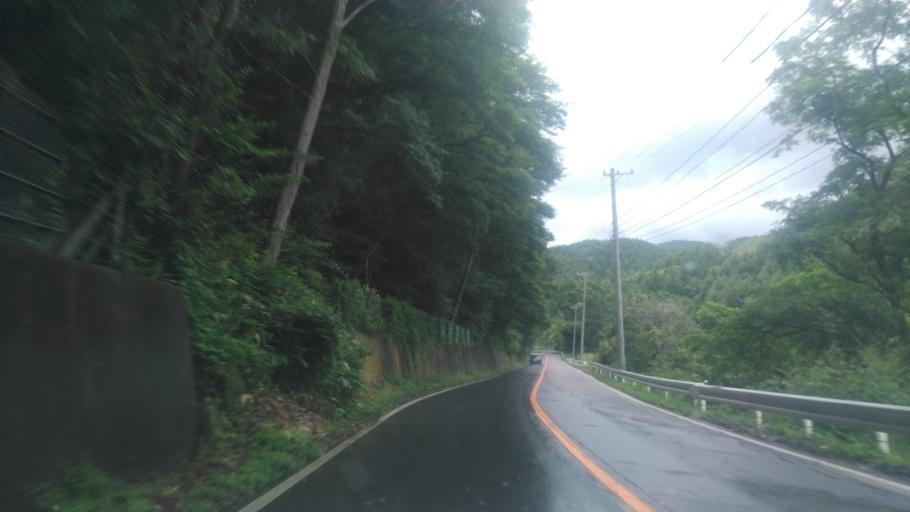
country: JP
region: Nagano
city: Ueda
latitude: 36.4909
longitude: 138.3692
